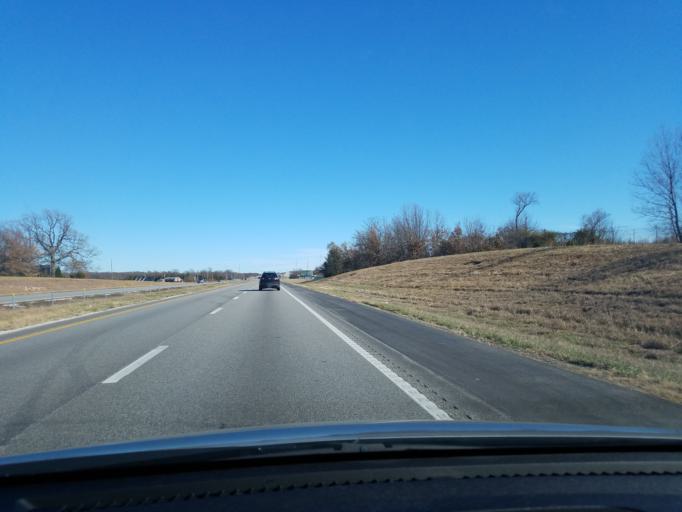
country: US
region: Missouri
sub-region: Greene County
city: Strafford
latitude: 37.2528
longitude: -93.1748
